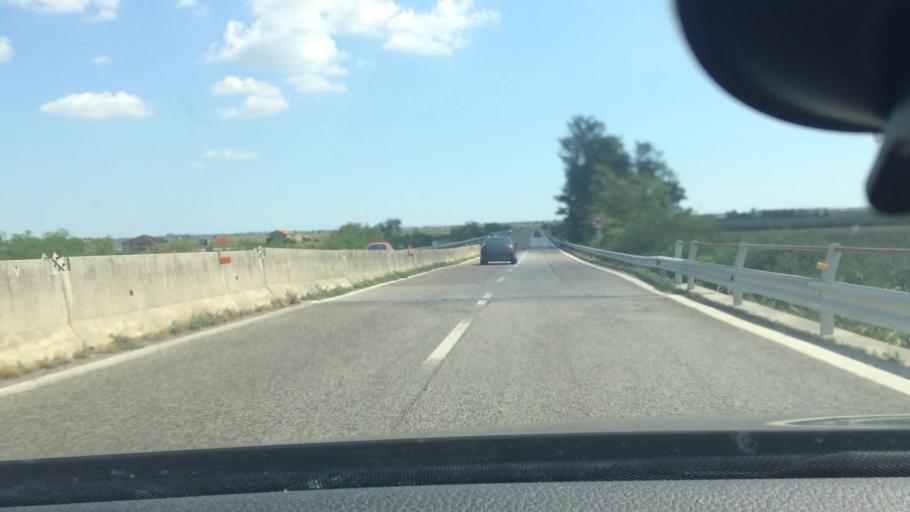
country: IT
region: Emilia-Romagna
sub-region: Provincia di Ferrara
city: Ostellato
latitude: 44.7560
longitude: 11.9574
